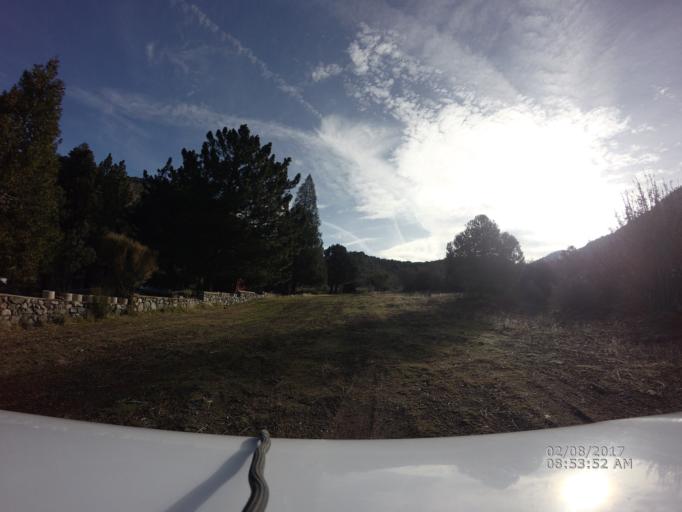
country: US
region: California
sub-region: San Bernardino County
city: Pinon Hills
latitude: 34.3943
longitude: -117.8077
